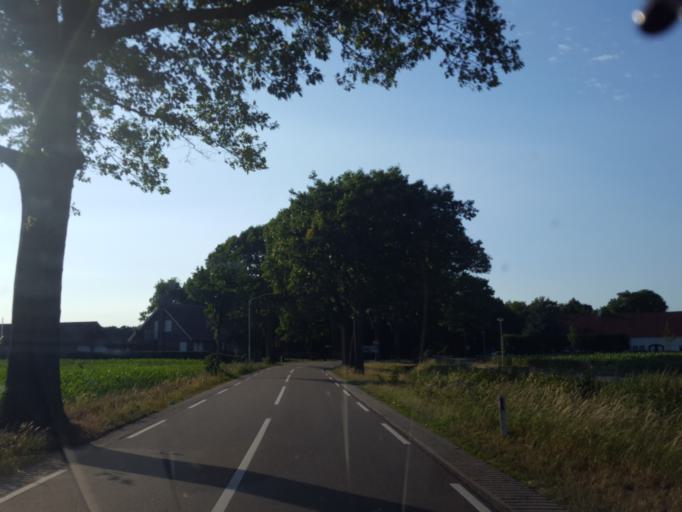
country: NL
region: Limburg
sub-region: Gemeente Leudal
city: Heythuysen
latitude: 51.3588
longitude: 5.8667
